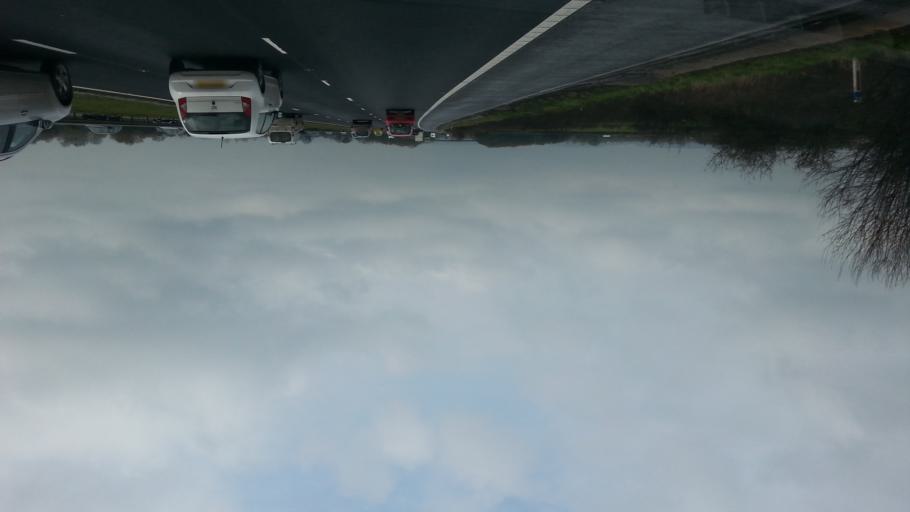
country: GB
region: England
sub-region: North Somerset
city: Kingston Seymour
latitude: 51.3855
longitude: -2.8694
